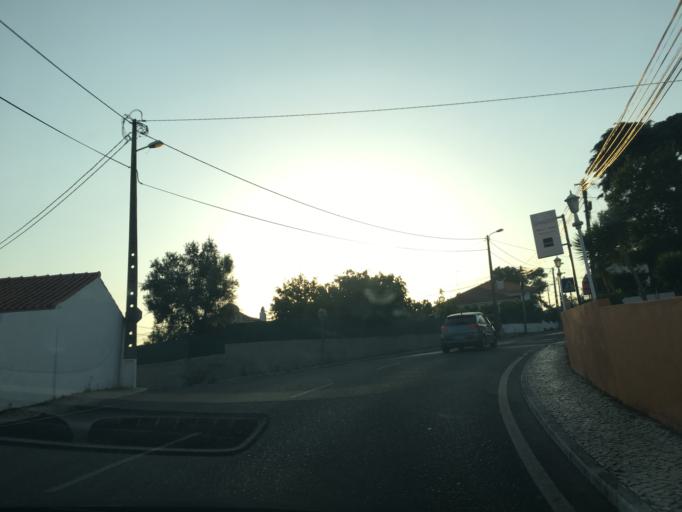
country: PT
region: Lisbon
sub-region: Sintra
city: Sintra
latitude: 38.8149
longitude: -9.3918
